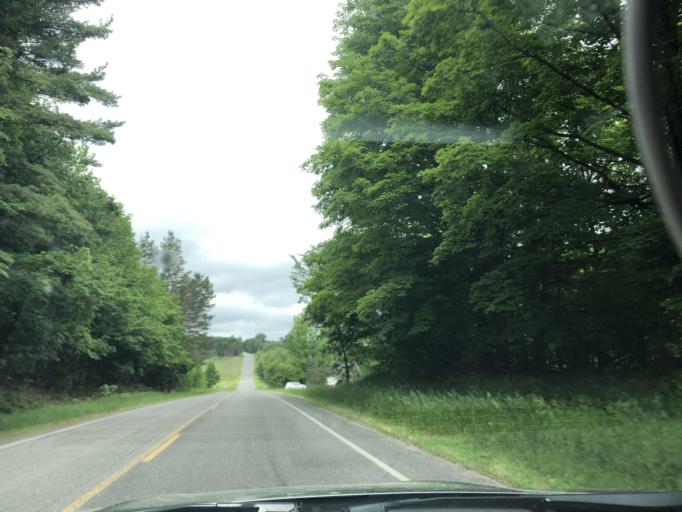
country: US
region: Michigan
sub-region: Missaukee County
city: Lake City
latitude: 44.4537
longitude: -85.2054
